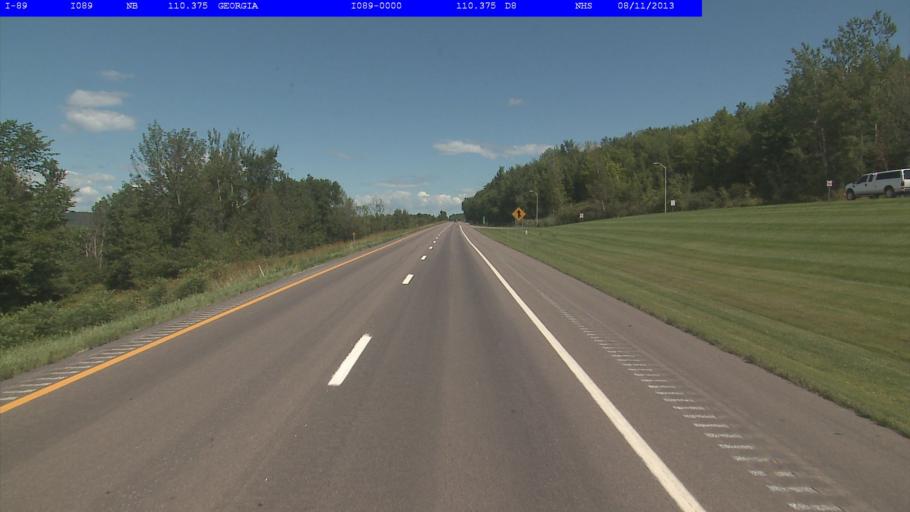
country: US
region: Vermont
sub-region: Franklin County
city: Saint Albans
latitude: 44.7464
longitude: -73.0787
